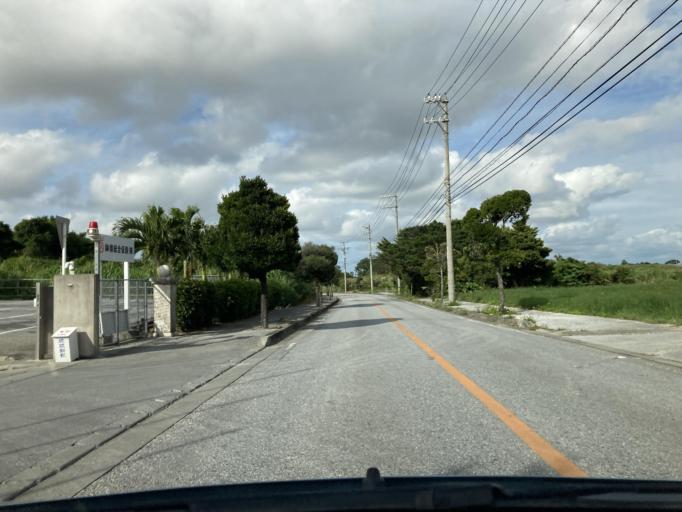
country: JP
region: Okinawa
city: Itoman
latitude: 26.1237
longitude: 127.7135
